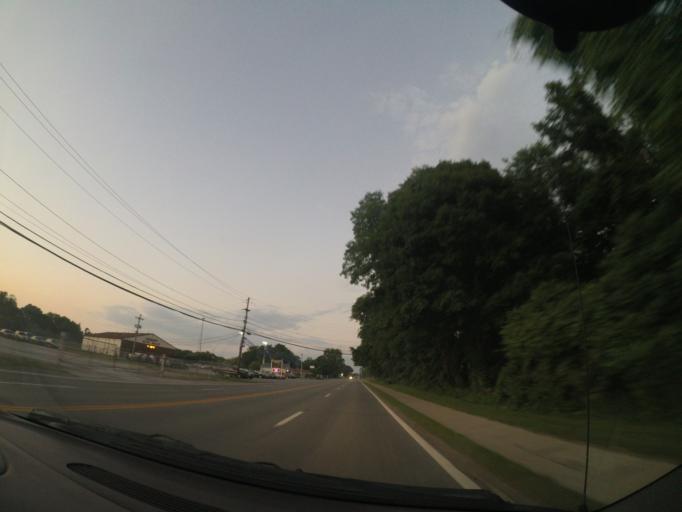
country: US
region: Ohio
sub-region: Lake County
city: North Madison
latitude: 41.7978
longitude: -81.0830
